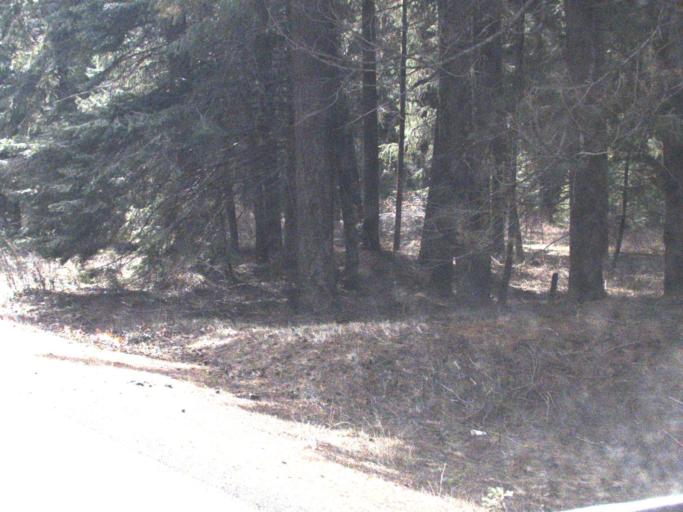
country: US
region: Washington
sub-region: Kittitas County
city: Cle Elum
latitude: 46.9747
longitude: -121.0948
